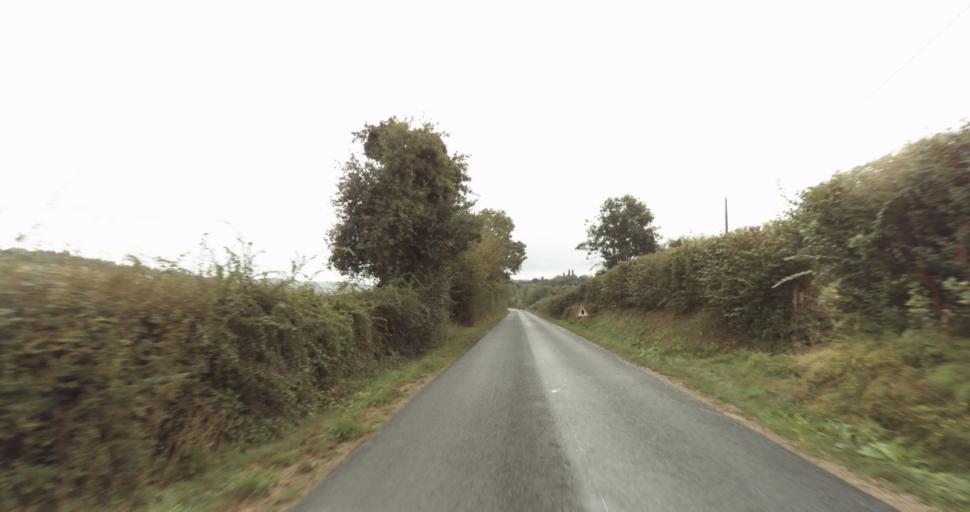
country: FR
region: Lower Normandy
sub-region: Departement de l'Orne
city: Vimoutiers
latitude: 48.8934
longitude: 0.2114
